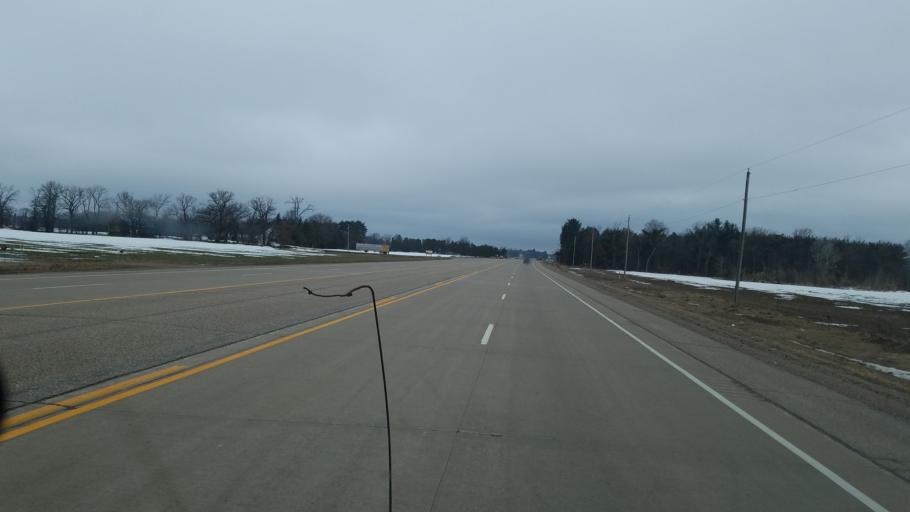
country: US
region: Wisconsin
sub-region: Portage County
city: Whiting
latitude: 44.5224
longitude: -89.4637
